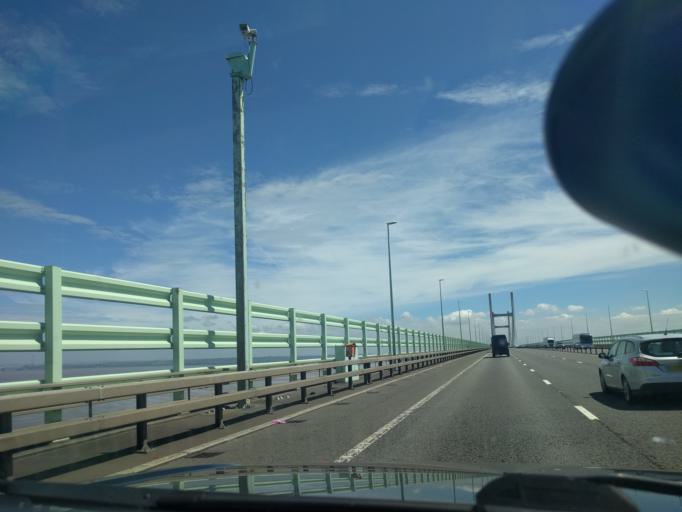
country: GB
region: Wales
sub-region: Monmouthshire
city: Caldicot
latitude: 51.5785
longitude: -2.7164
